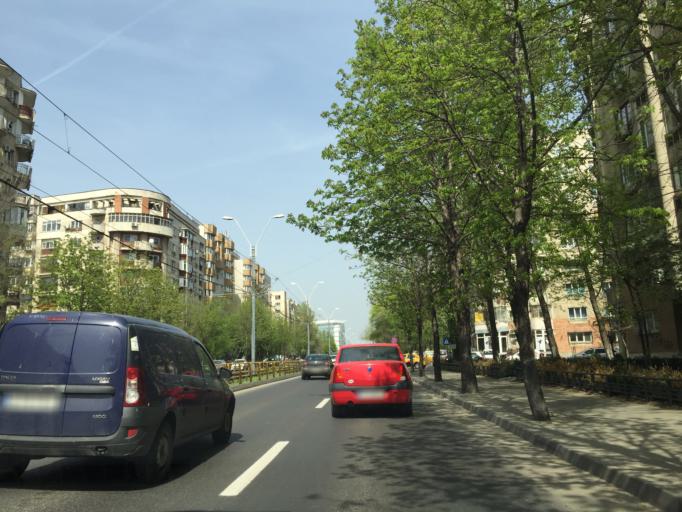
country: RO
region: Ilfov
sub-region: Comuna Chiajna
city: Rosu
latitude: 44.4383
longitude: 26.0354
